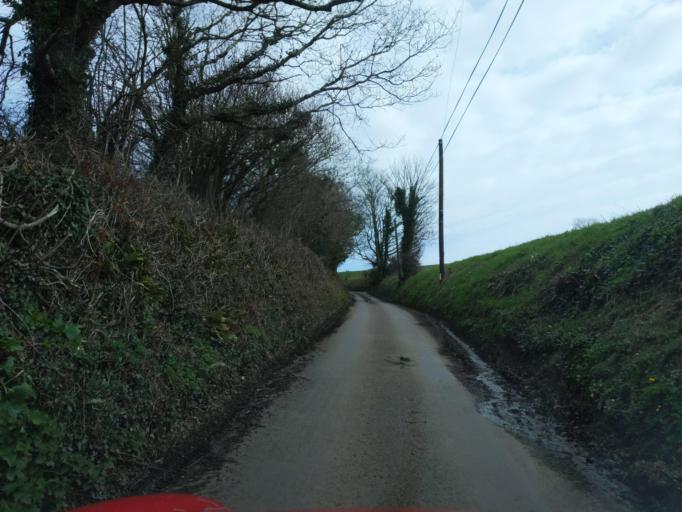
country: GB
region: England
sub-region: Devon
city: Yealmpton
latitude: 50.3633
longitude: -4.0083
